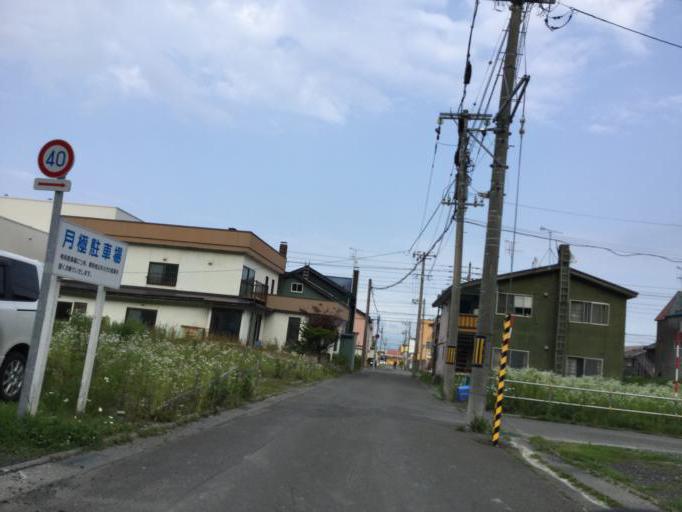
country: JP
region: Hokkaido
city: Wakkanai
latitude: 45.4118
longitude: 141.6732
